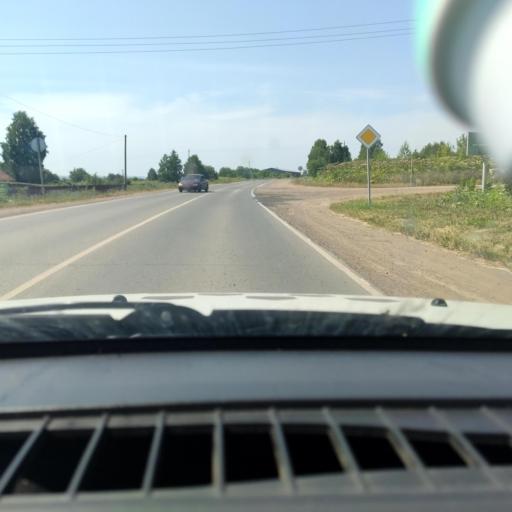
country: RU
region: Perm
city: Okhansk
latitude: 57.7112
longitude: 55.3372
